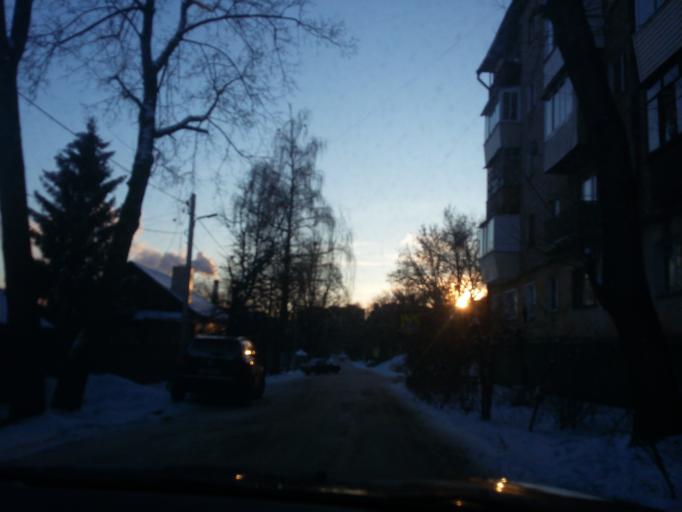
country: RU
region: Tula
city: Mendeleyevskiy
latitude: 54.1628
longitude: 37.5968
